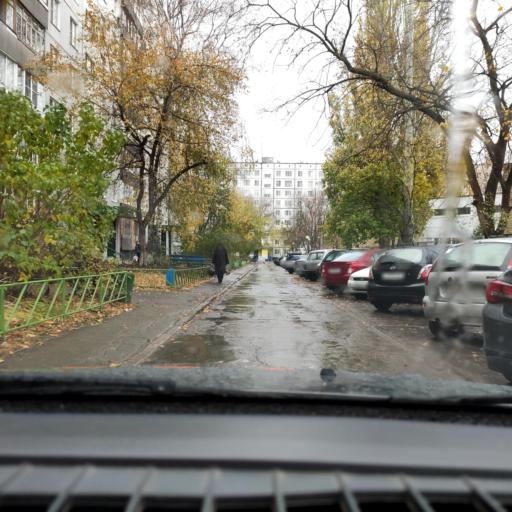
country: RU
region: Samara
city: Tol'yatti
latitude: 53.5097
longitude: 49.2652
